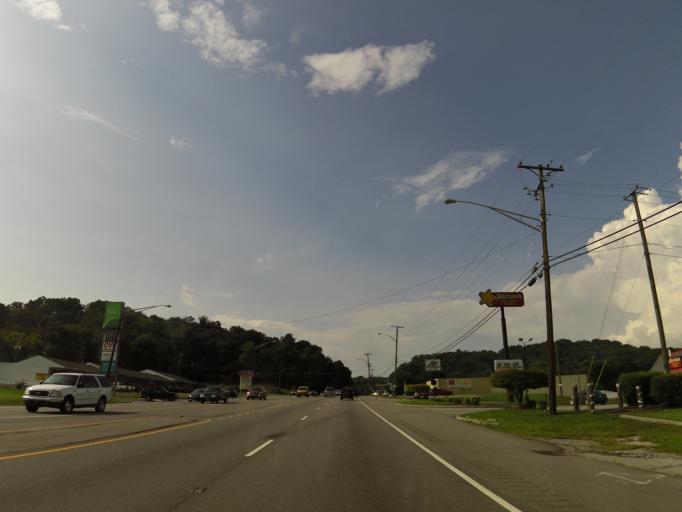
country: US
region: Tennessee
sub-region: Knox County
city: Knoxville
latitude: 35.9123
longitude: -83.9554
